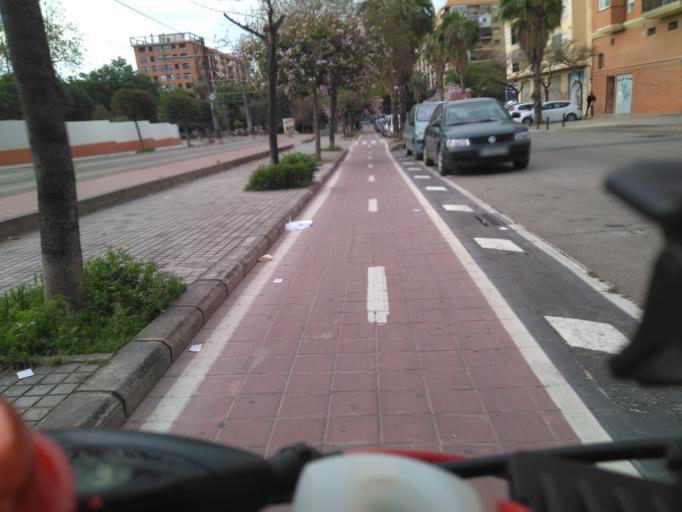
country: ES
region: Valencia
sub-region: Provincia de Valencia
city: Valencia
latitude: 39.4870
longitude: -0.3837
